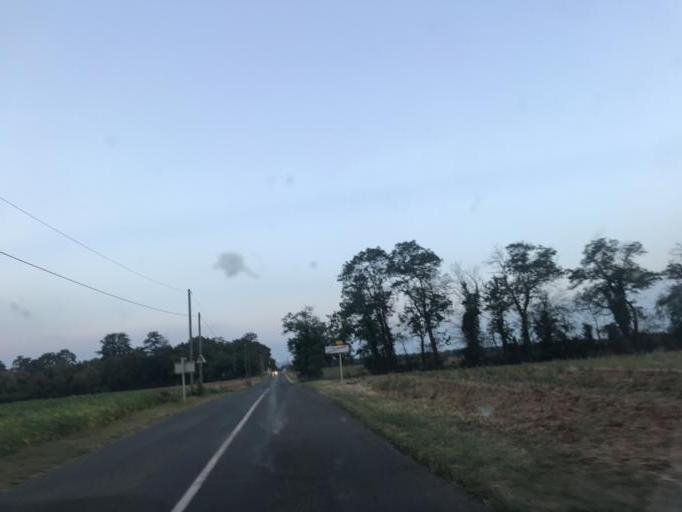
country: FR
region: Rhone-Alpes
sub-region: Departement de l'Ain
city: Chazey-sur-Ain
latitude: 45.8683
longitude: 5.2800
